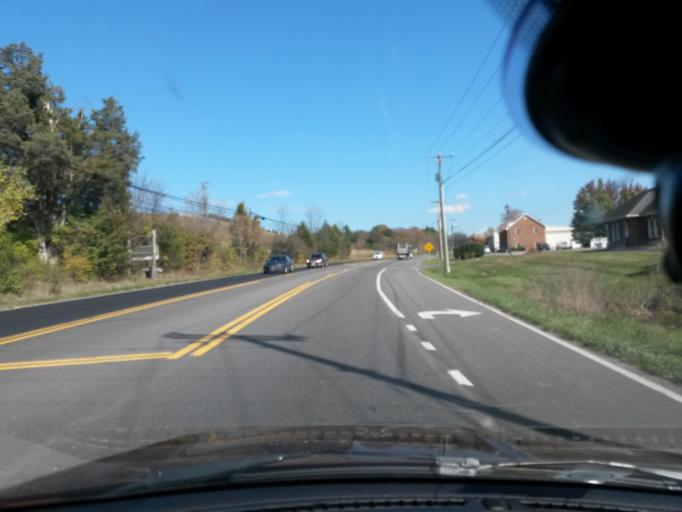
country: US
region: Virginia
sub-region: Botetourt County
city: Cloverdale
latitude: 37.3621
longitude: -79.9222
